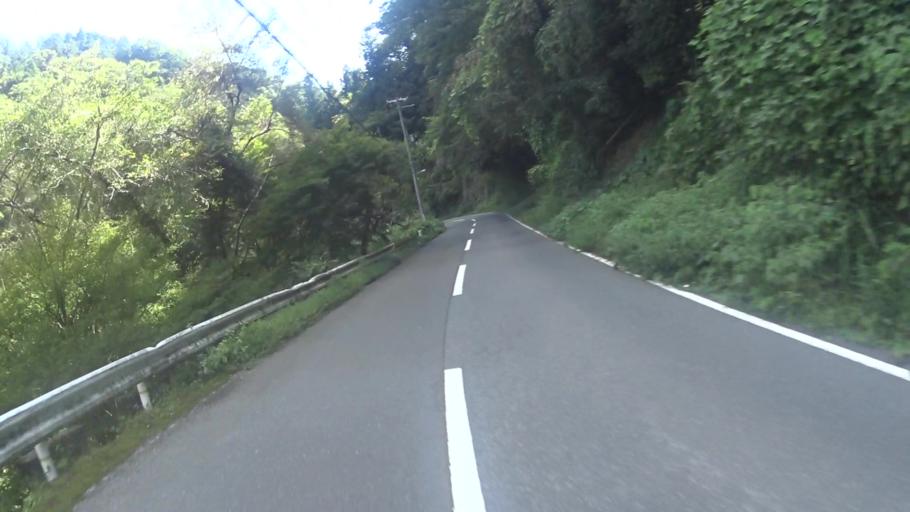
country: JP
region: Mie
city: Nabari
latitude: 34.7071
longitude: 136.0203
